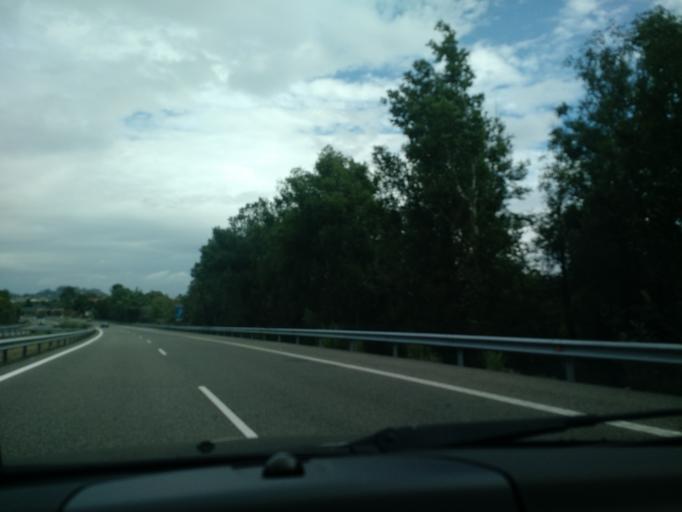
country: ES
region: Galicia
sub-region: Provincia da Coruna
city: Abegondo
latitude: 43.2522
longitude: -8.2544
